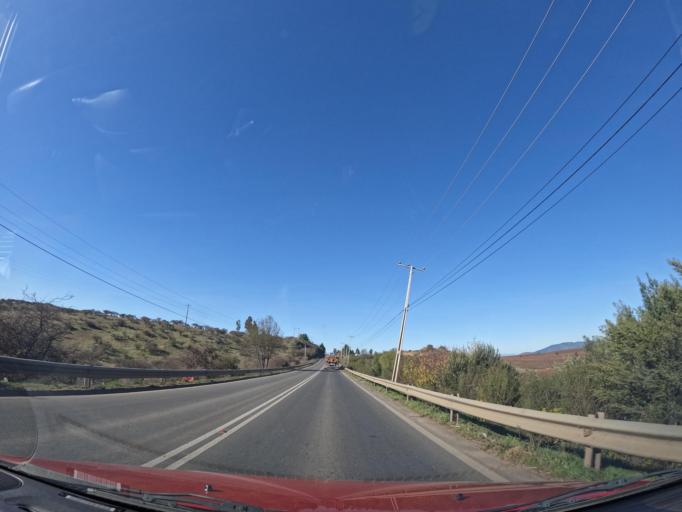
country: CL
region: Maule
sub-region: Provincia de Cauquenes
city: Cauquenes
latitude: -35.9604
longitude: -72.2586
